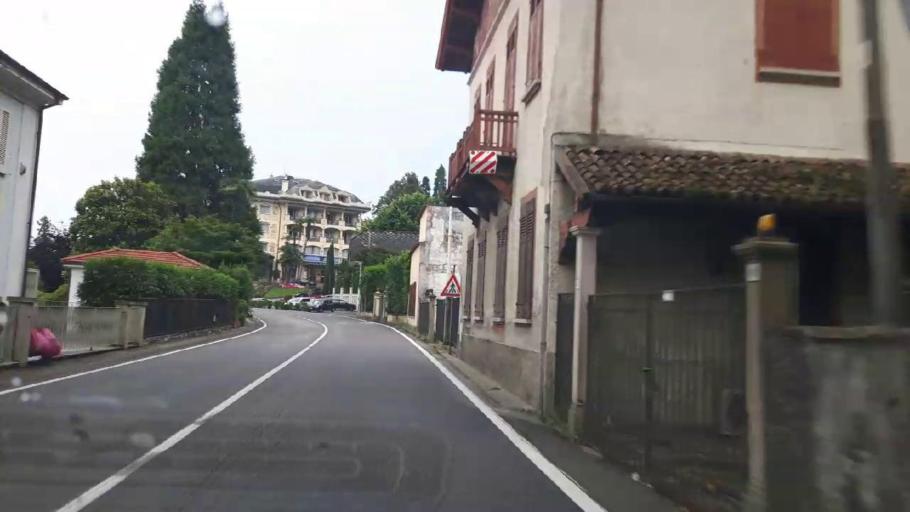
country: IT
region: Piedmont
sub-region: Provincia Verbano-Cusio-Ossola
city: Baveno
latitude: 45.8939
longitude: 8.5159
